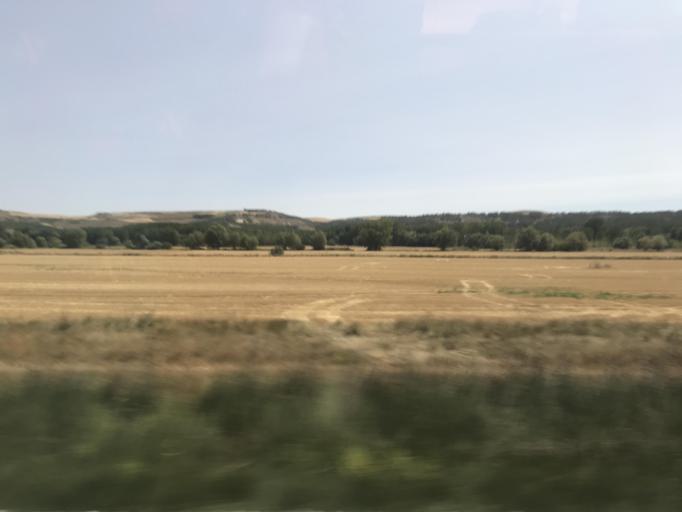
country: ES
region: Castille and Leon
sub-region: Provincia de Burgos
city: Pampliega
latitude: 42.2240
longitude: -3.9904
